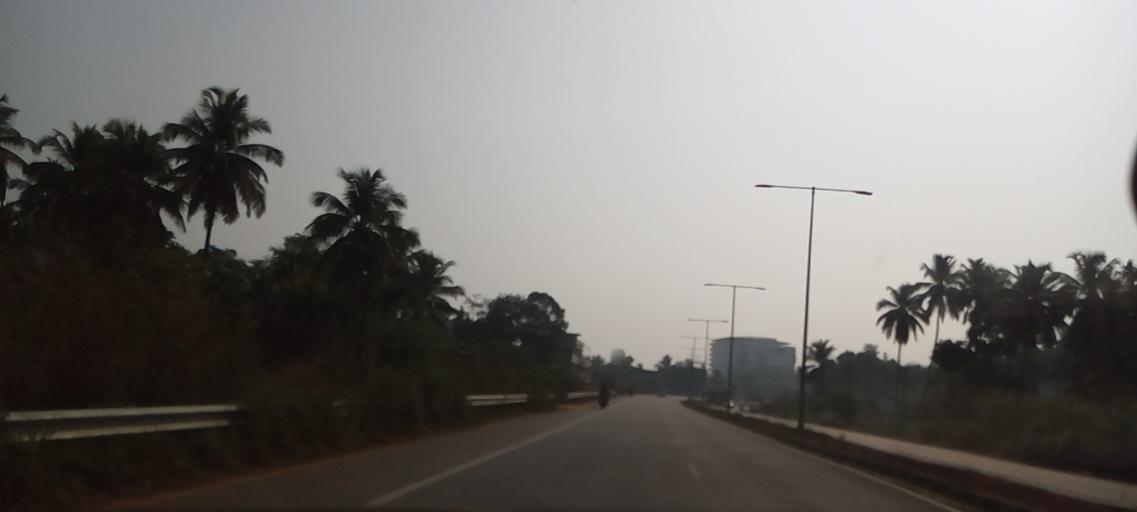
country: IN
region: Karnataka
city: Gangolli
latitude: 13.6784
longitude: 74.6950
